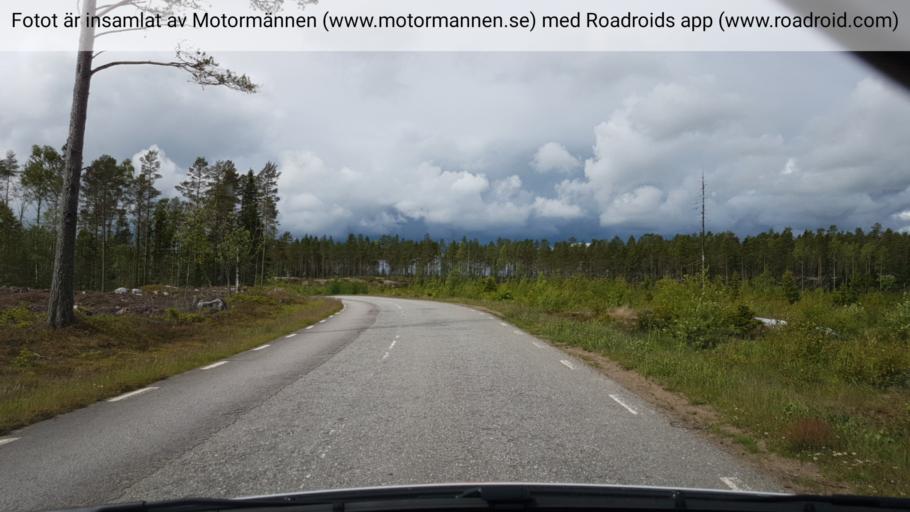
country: SE
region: Vaesterbotten
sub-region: Umea Kommun
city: Hoernefors
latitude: 63.5630
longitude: 19.7555
